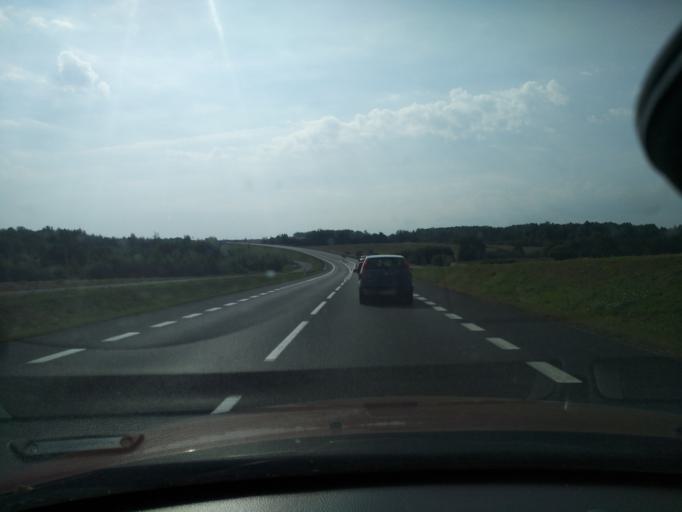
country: PL
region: Lower Silesian Voivodeship
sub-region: Powiat lwowecki
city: Gryfow Slaski
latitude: 51.0046
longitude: 15.4522
